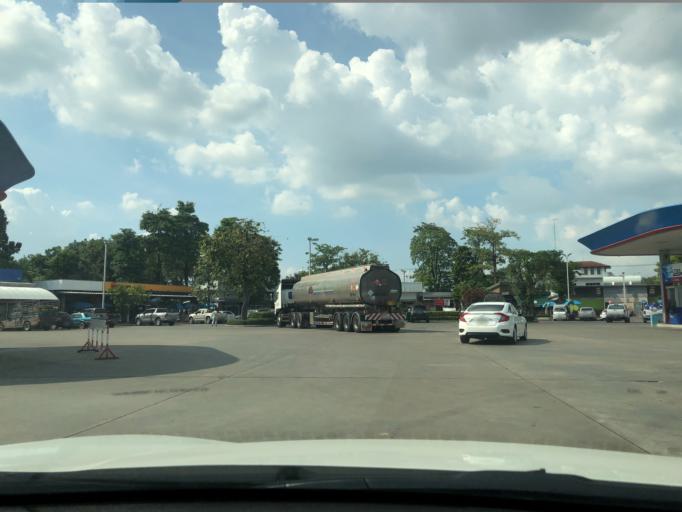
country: TH
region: Nakhon Sawan
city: Krok Phra
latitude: 15.5768
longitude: 100.1240
